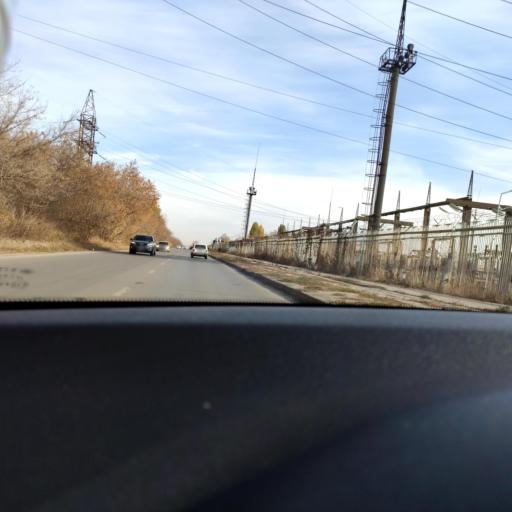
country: RU
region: Samara
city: Petra-Dubrava
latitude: 53.2528
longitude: 50.2740
